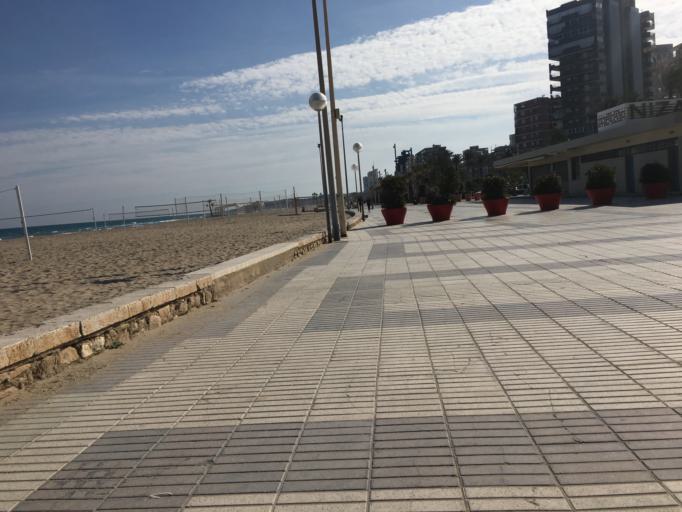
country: ES
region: Valencia
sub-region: Provincia de Alicante
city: San Juan de Alicante
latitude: 38.3763
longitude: -0.4101
